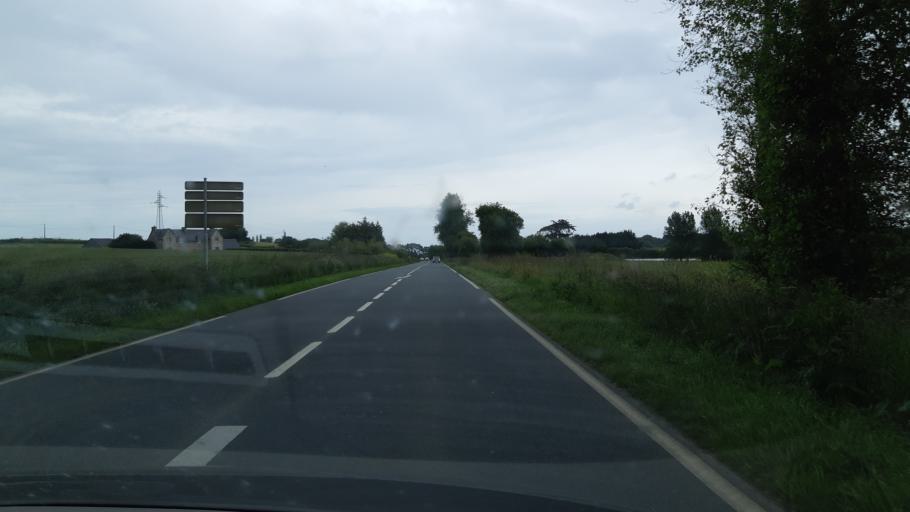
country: FR
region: Brittany
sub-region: Departement du Finistere
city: Plougoulm
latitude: 48.6492
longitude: -4.0413
